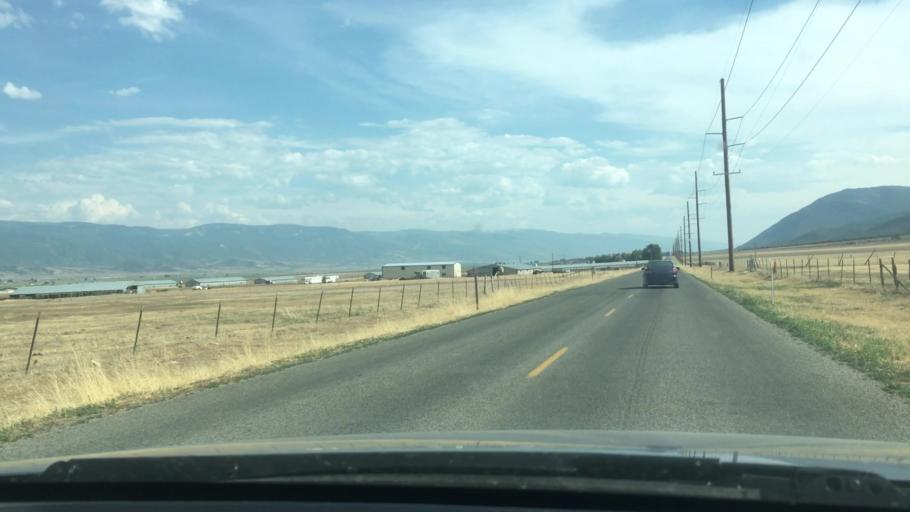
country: US
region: Utah
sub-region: Sanpete County
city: Moroni
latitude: 39.5334
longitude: -111.6398
